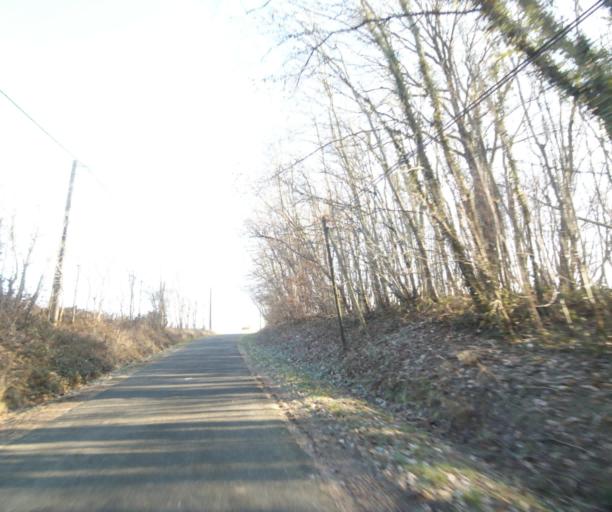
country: FR
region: Champagne-Ardenne
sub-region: Departement de la Haute-Marne
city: Bienville
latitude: 48.5078
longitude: 5.0311
